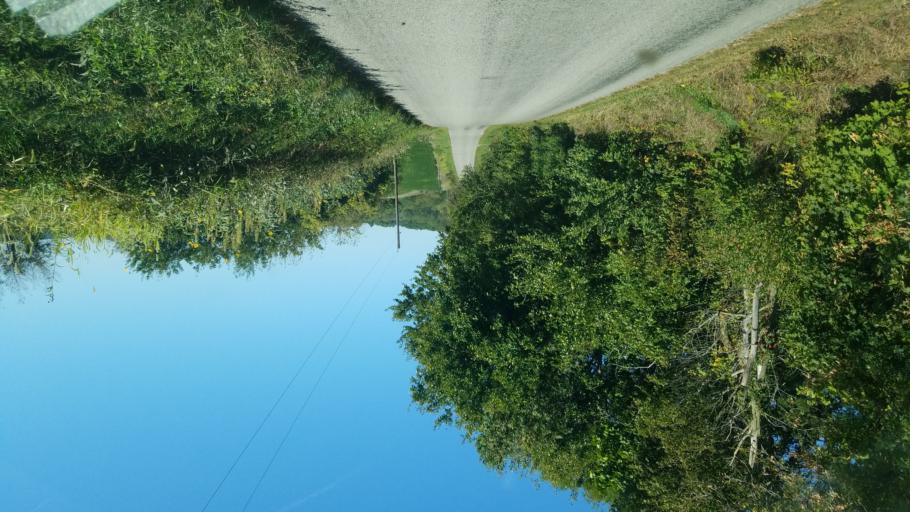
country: US
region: Ohio
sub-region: Logan County
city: West Liberty
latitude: 40.3052
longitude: -83.7282
